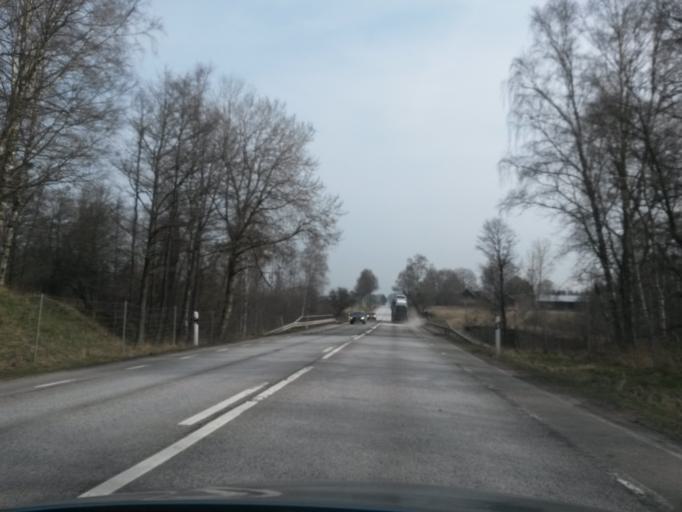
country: SE
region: Vaestra Goetaland
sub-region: Gullspangs Kommun
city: Hova
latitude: 58.8658
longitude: 14.2298
